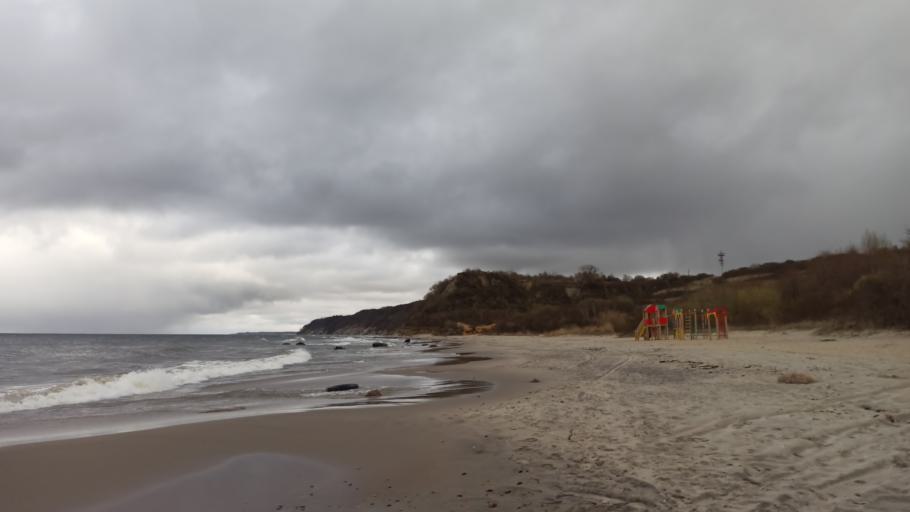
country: RU
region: Kaliningrad
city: Donskoye
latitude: 54.9477
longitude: 20.0208
